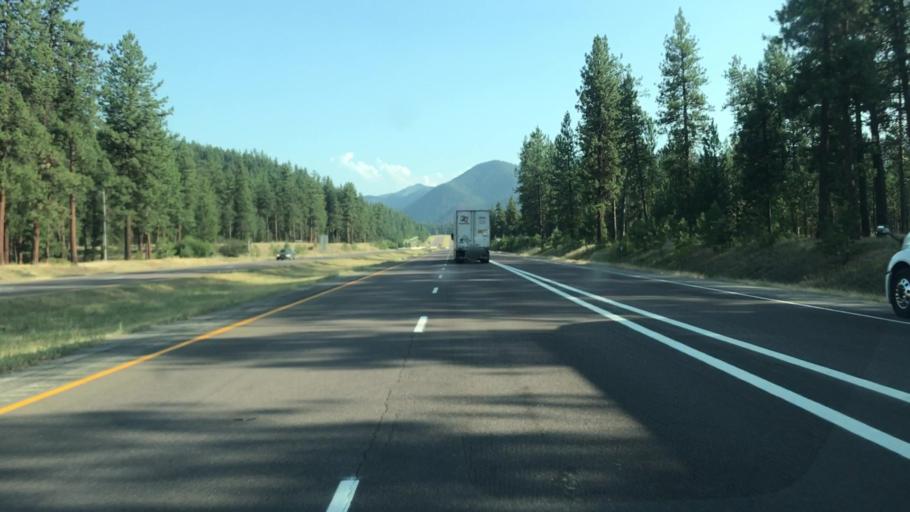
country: US
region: Montana
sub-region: Mineral County
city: Superior
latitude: 47.0740
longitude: -114.7659
